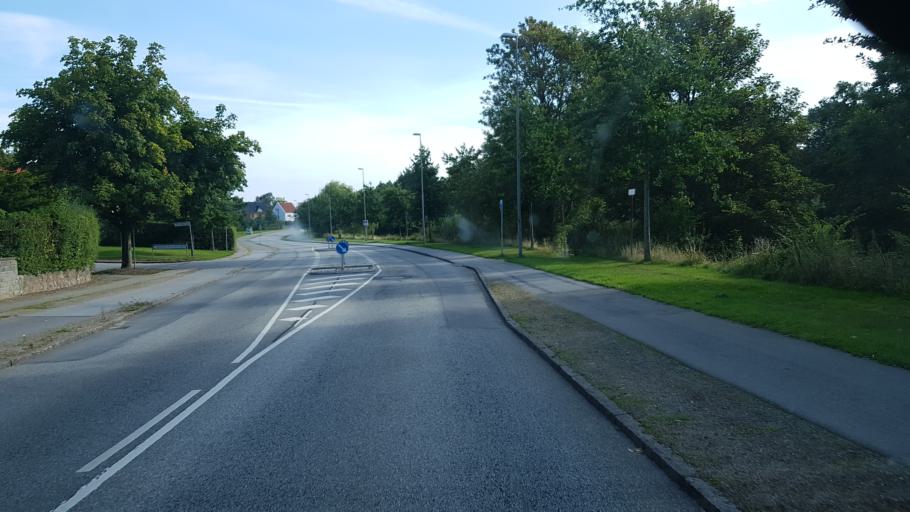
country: DK
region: South Denmark
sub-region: Haderslev Kommune
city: Haderslev
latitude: 55.2385
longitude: 9.4932
